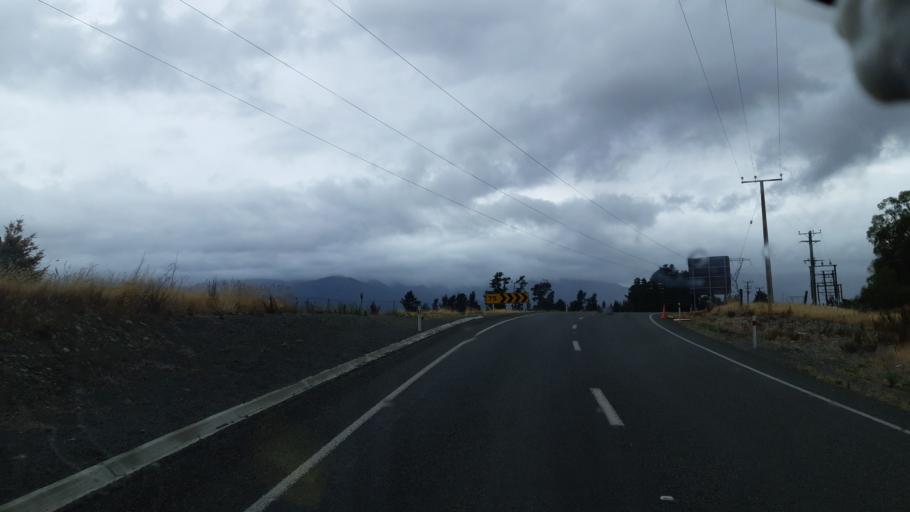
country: NZ
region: Canterbury
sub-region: Hurunui District
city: Amberley
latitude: -42.5886
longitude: 172.7771
